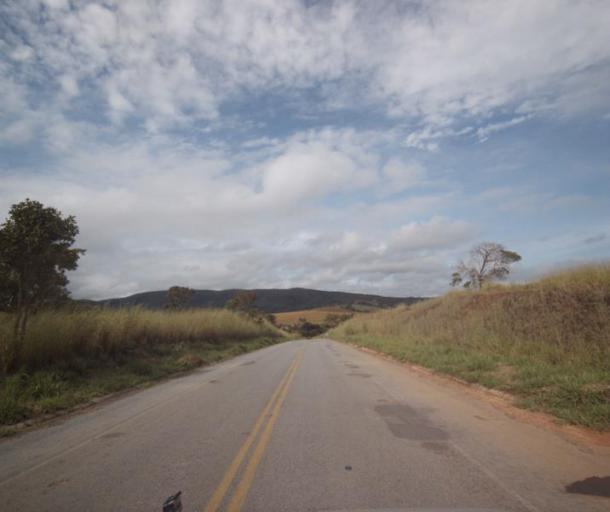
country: BR
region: Goias
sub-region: Pirenopolis
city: Pirenopolis
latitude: -15.6801
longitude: -48.7059
